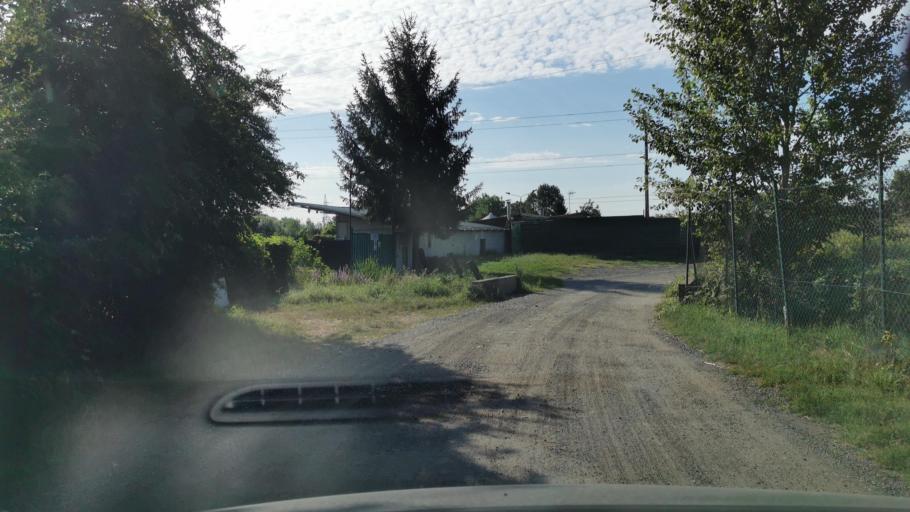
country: IT
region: Piedmont
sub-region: Provincia di Torino
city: Settimo Torinese
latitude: 45.1657
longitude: 7.7752
